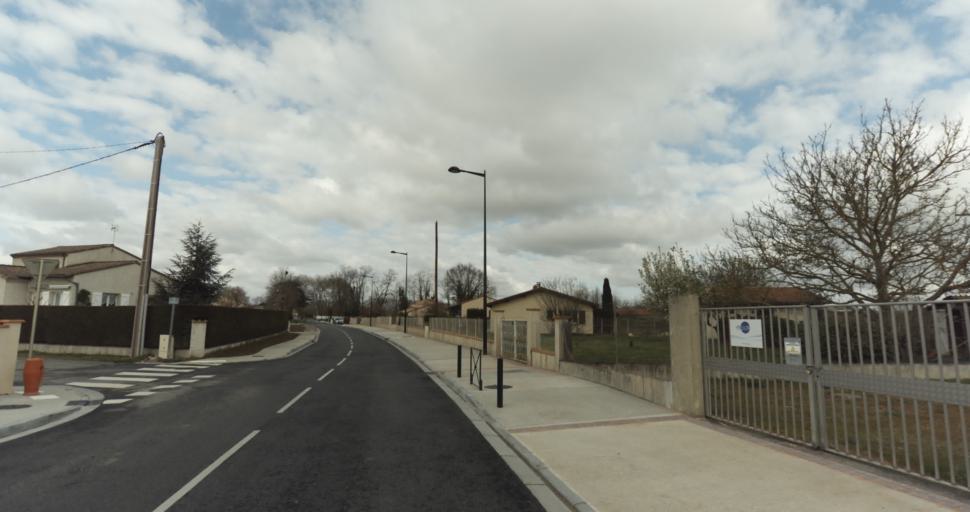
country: FR
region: Midi-Pyrenees
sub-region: Departement de la Haute-Garonne
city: Auterive
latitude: 43.3557
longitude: 1.4626
